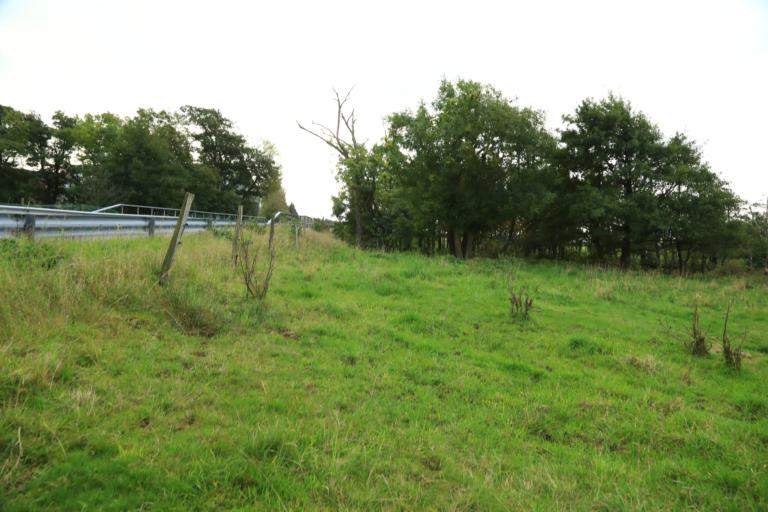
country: SE
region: Halland
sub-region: Varbergs Kommun
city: Traslovslage
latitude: 57.0270
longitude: 12.3337
